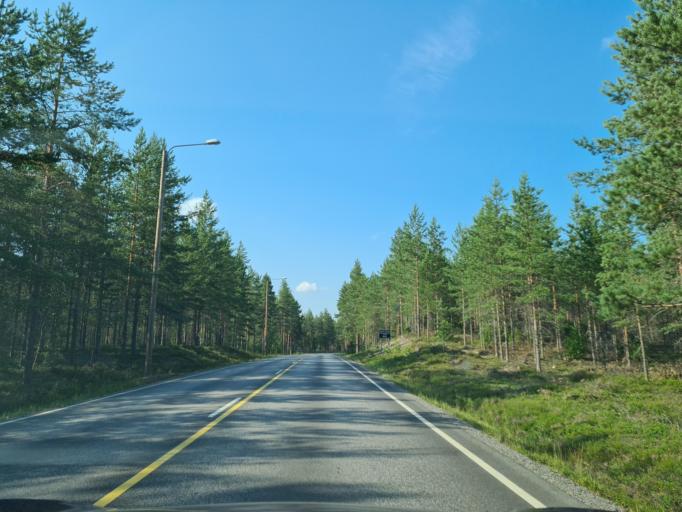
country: FI
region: Satakunta
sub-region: Pohjois-Satakunta
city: Karvia
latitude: 62.0718
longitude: 22.5073
